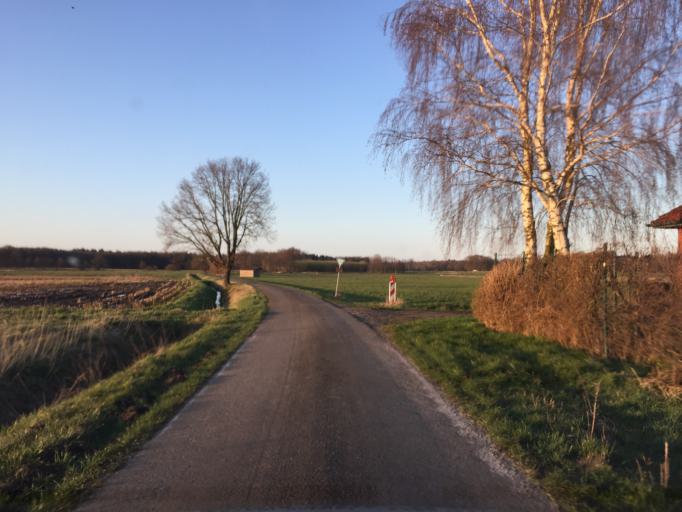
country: DE
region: Lower Saxony
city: Varrel
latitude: 52.6593
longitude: 8.7470
